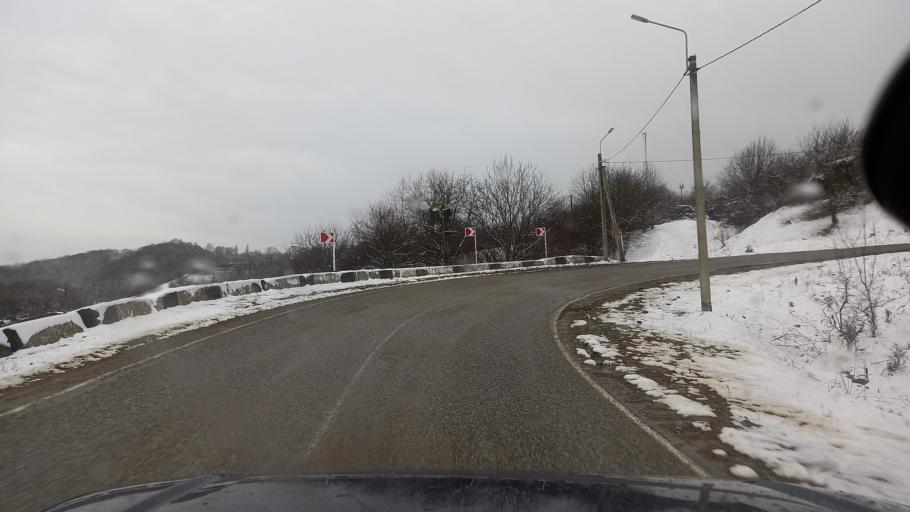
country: RU
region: Adygeya
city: Abadzekhskaya
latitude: 44.3554
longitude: 40.3101
